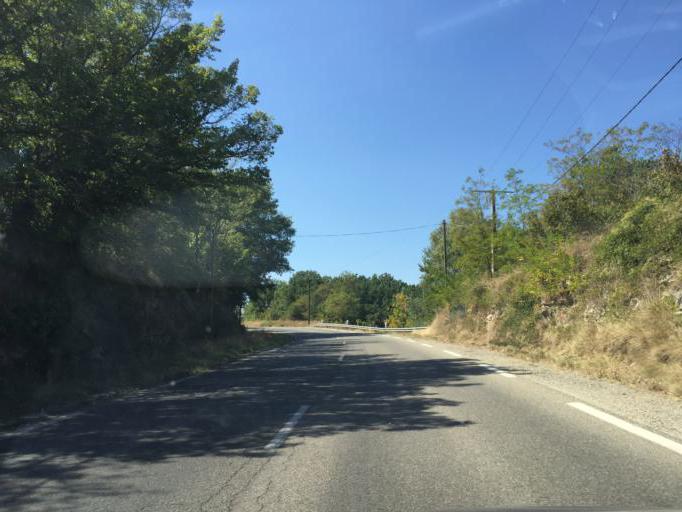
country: FR
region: Provence-Alpes-Cote d'Azur
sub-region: Departement des Alpes-de-Haute-Provence
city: Forcalquier
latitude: 43.9574
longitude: 5.8035
